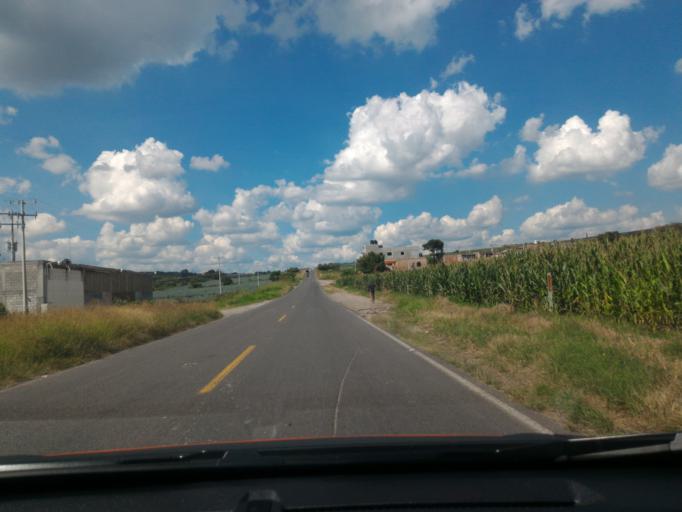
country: MX
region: Guanajuato
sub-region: Penjamo
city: Estacion la Piedad
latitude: 20.4182
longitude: -101.9946
